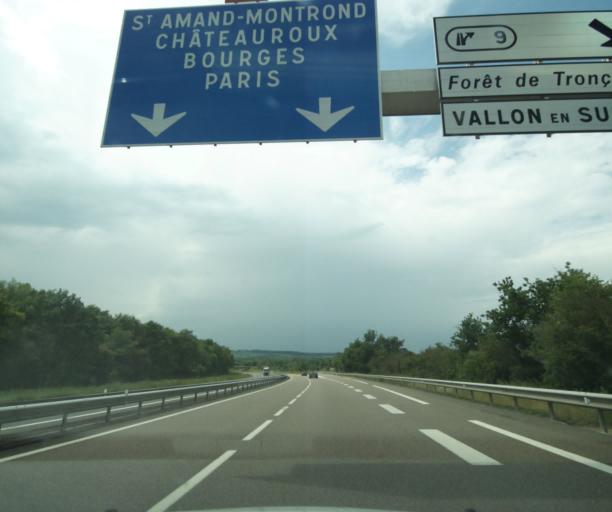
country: FR
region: Auvergne
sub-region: Departement de l'Allier
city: Vallon-en-Sully
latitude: 46.5084
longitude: 2.6371
